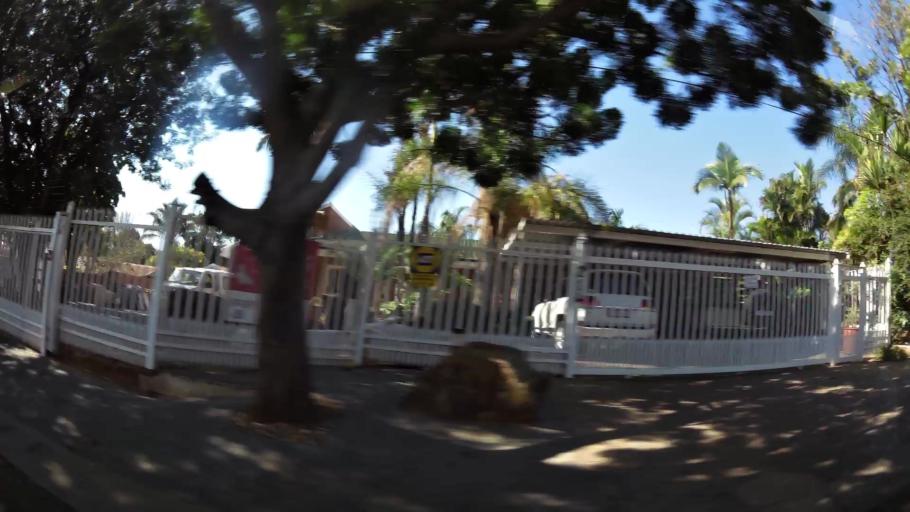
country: ZA
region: Gauteng
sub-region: City of Tshwane Metropolitan Municipality
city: Pretoria
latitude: -25.6845
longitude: 28.2475
